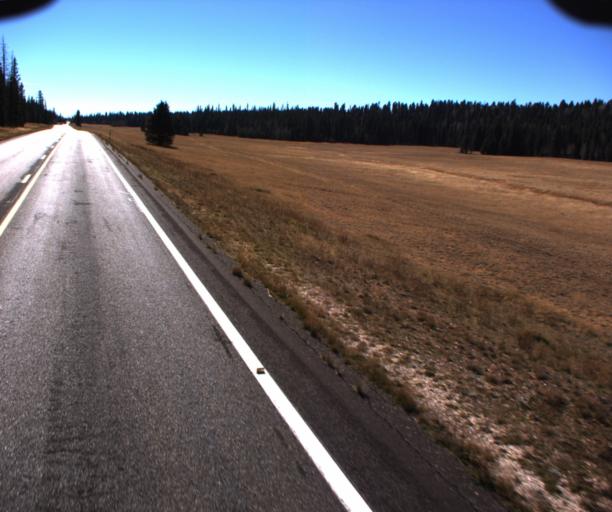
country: US
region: Arizona
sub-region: Coconino County
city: Grand Canyon
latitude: 36.3520
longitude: -112.1181
